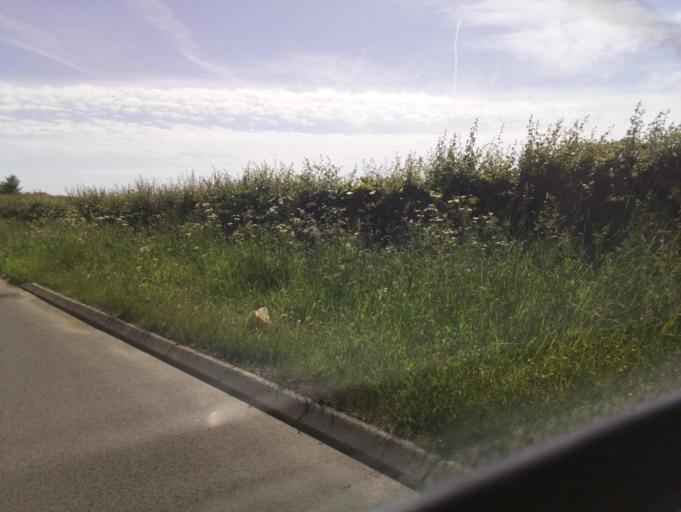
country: GB
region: England
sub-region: Devon
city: Starcross
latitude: 50.6611
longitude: -3.4249
